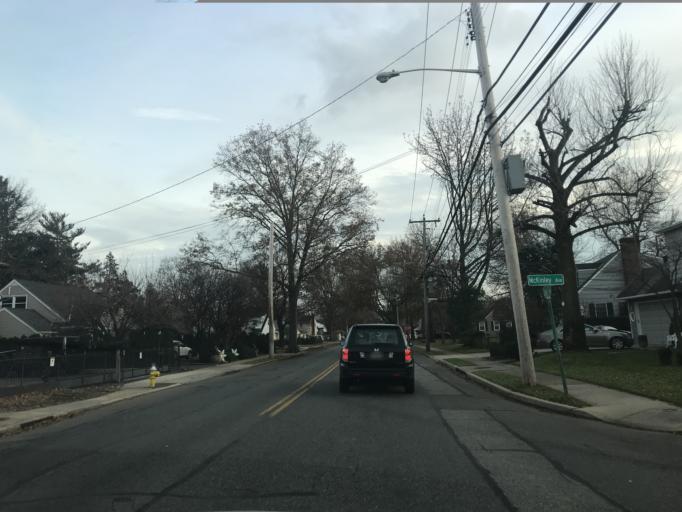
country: US
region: New York
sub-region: Nassau County
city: Carle Place
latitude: 40.7585
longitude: -73.6002
